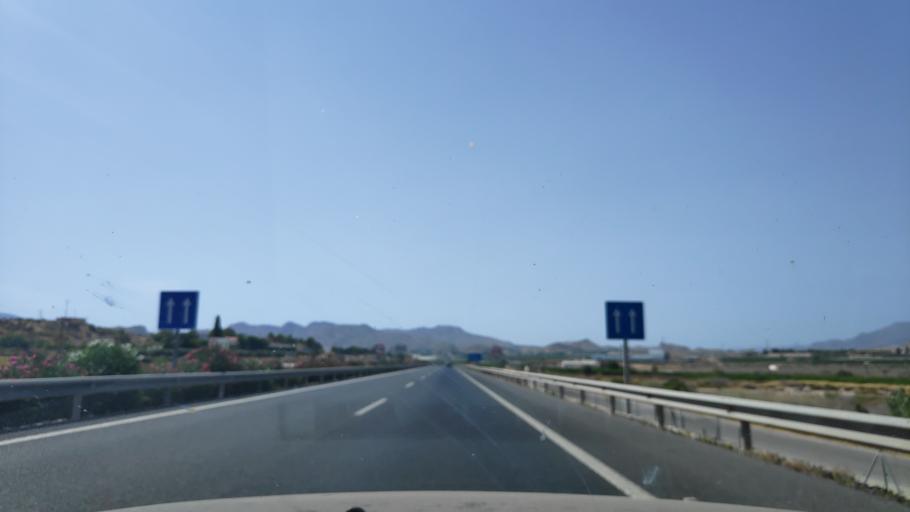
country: ES
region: Murcia
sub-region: Murcia
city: Archena
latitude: 38.1286
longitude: -1.2605
